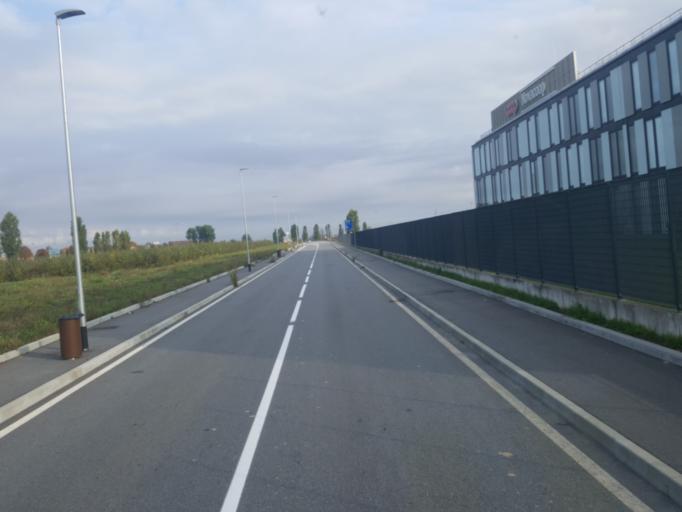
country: IT
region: Piedmont
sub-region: Provincia di Vercelli
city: Asigliano Vercellese
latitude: 45.2929
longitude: 8.3907
